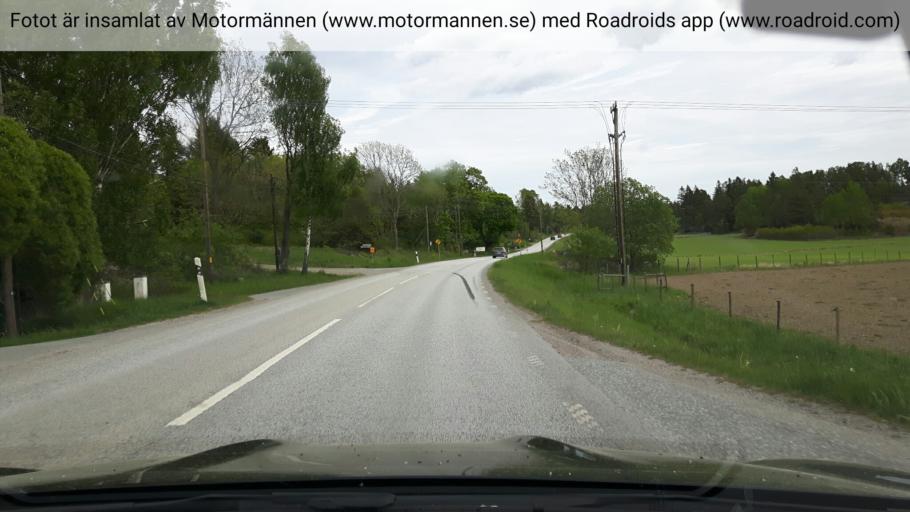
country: SE
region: Stockholm
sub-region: Vaxholms Kommun
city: Resaro
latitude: 59.5485
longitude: 18.5063
